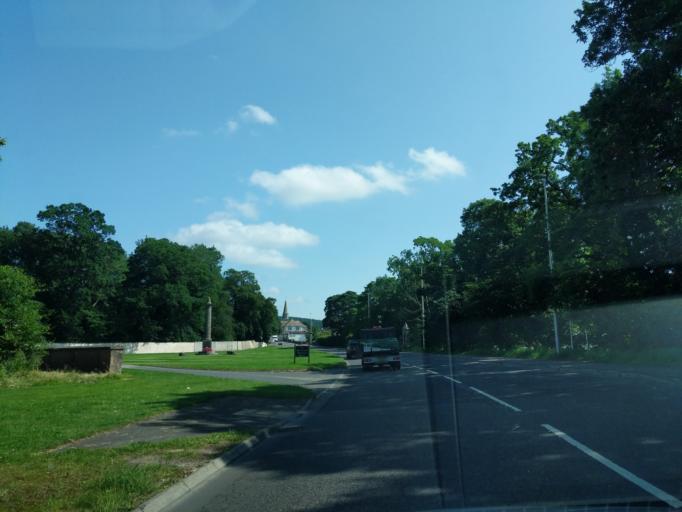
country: GB
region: Scotland
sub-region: Moray
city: Fochabers
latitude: 57.6164
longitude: -3.1031
